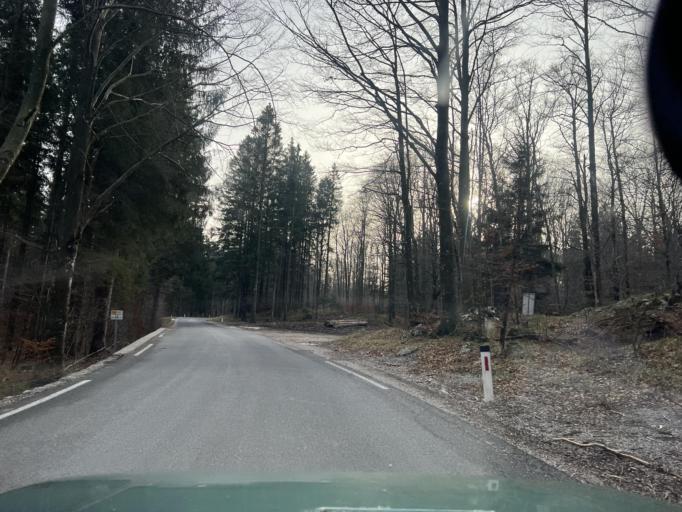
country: SI
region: Nova Gorica
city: Sempas
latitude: 45.9865
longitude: 13.7600
